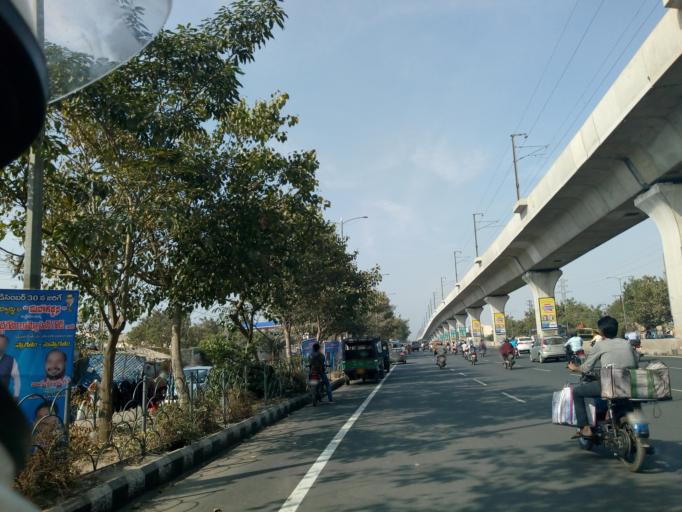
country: IN
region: Telangana
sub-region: Rangareddi
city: Lal Bahadur Nagar
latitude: 17.3519
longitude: 78.5464
